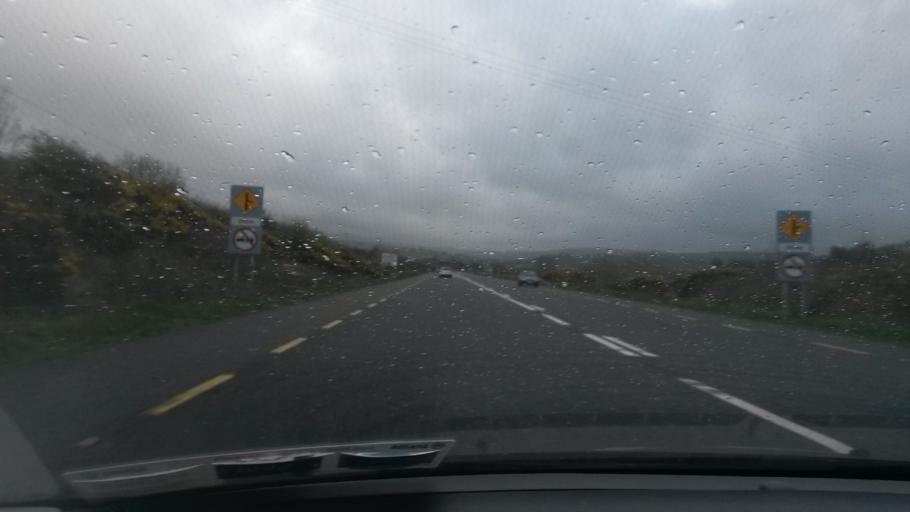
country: IE
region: Munster
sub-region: County Limerick
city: Abbeyfeale
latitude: 52.3208
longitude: -9.3594
